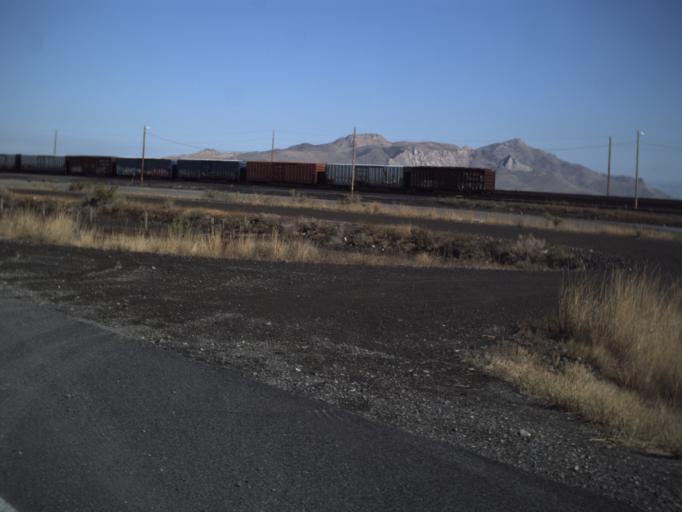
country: US
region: Utah
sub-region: Tooele County
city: Grantsville
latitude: 40.6864
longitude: -112.4425
